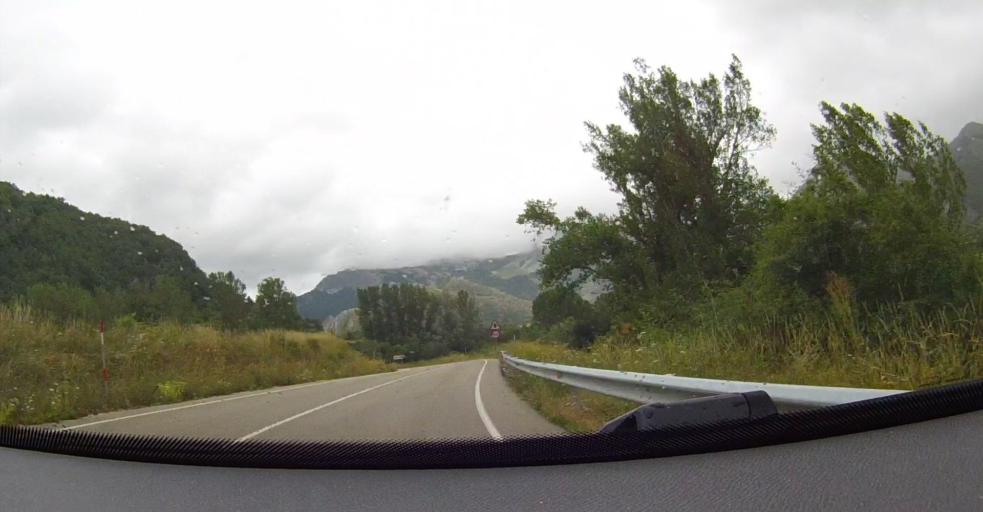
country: ES
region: Castille and Leon
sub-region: Provincia de Leon
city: Buron
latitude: 43.0326
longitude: -5.0765
